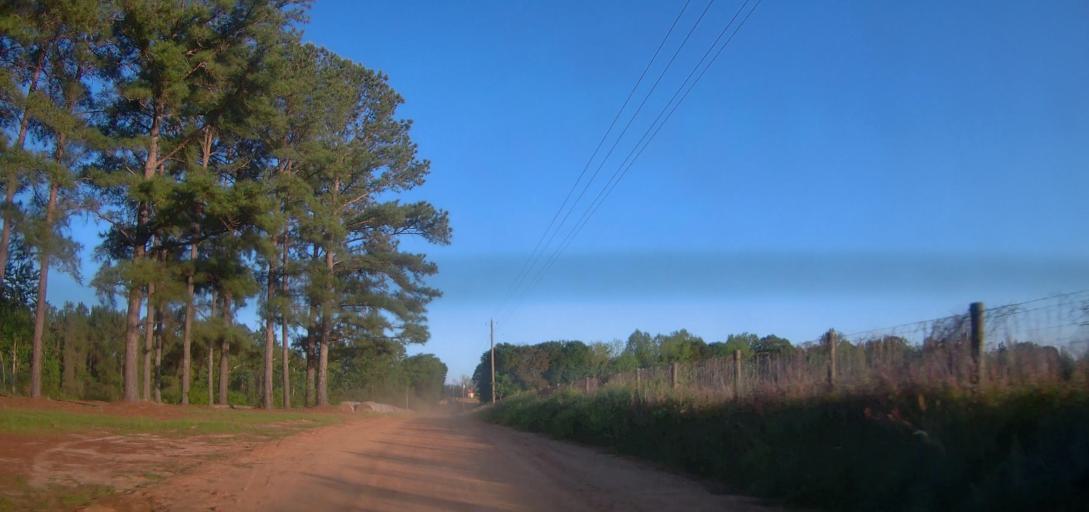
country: US
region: Georgia
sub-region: Irwin County
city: Ocilla
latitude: 31.6467
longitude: -83.2241
